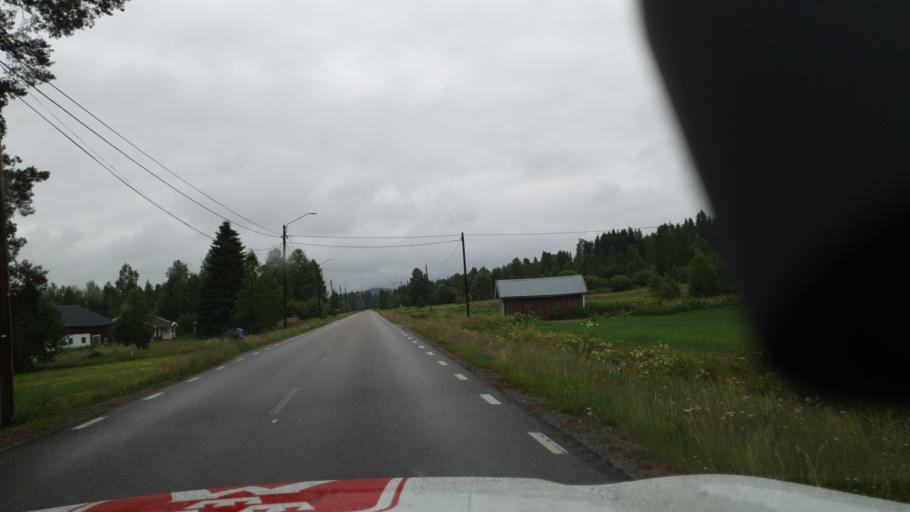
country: SE
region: Vaesterbotten
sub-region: Vannas Kommun
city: Vannasby
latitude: 63.7917
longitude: 19.8573
